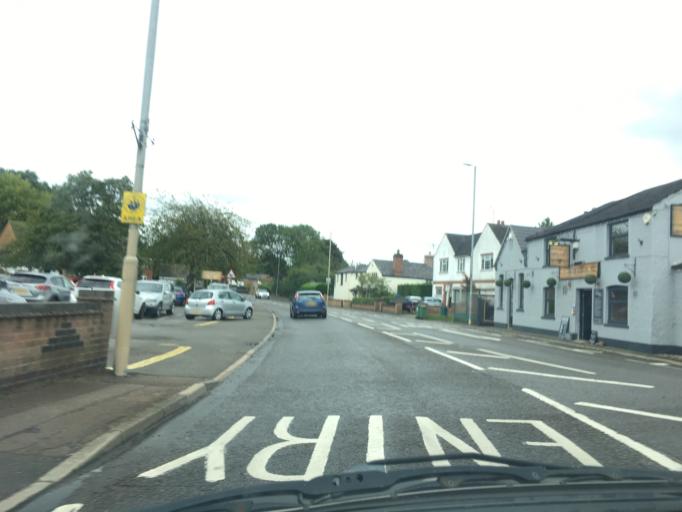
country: GB
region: England
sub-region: Leicestershire
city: Sapcote
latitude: 52.5216
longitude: -1.2937
